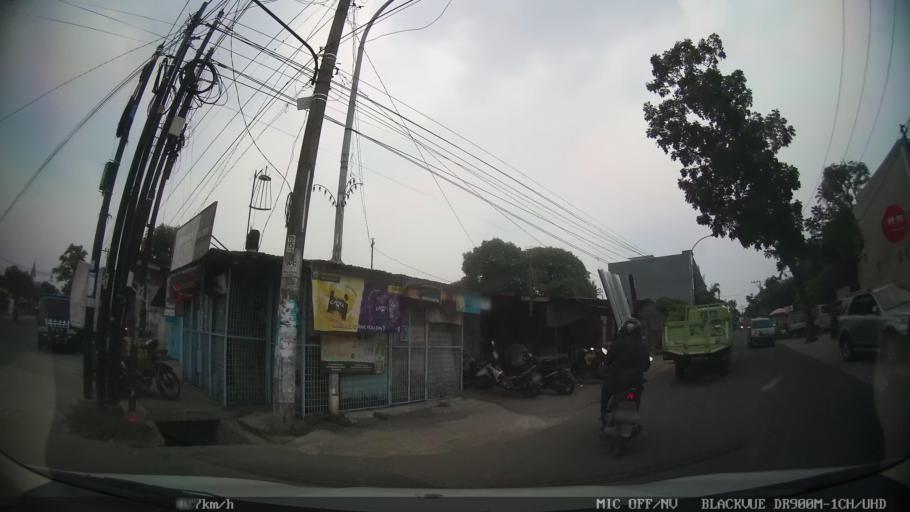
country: ID
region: North Sumatra
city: Medan
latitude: 3.5528
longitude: 98.7032
